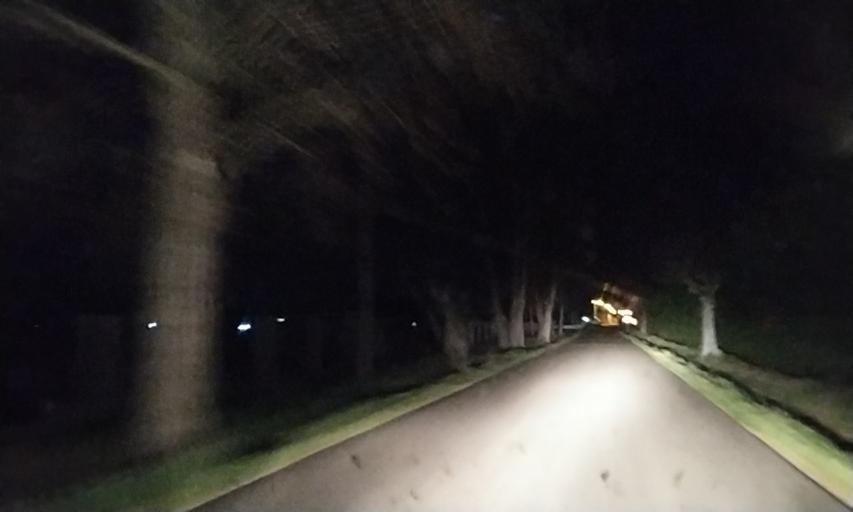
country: ES
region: Castille and Leon
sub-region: Provincia de Salamanca
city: Ciudad Rodrigo
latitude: 40.5870
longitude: -6.5443
